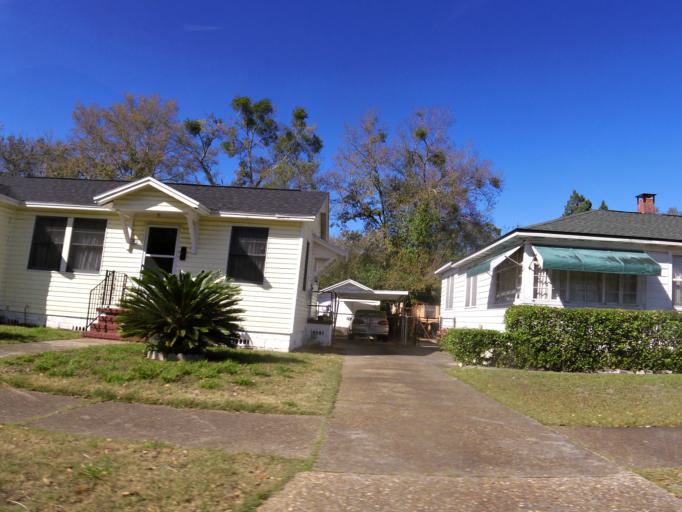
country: US
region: Florida
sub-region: Duval County
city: Jacksonville
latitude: 30.3593
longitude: -81.6498
